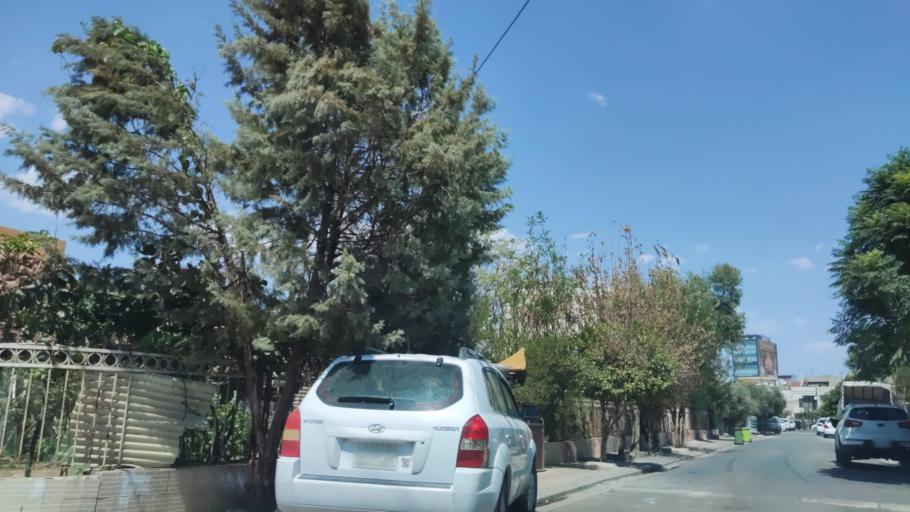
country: IQ
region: Arbil
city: Erbil
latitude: 36.1968
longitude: 44.0213
